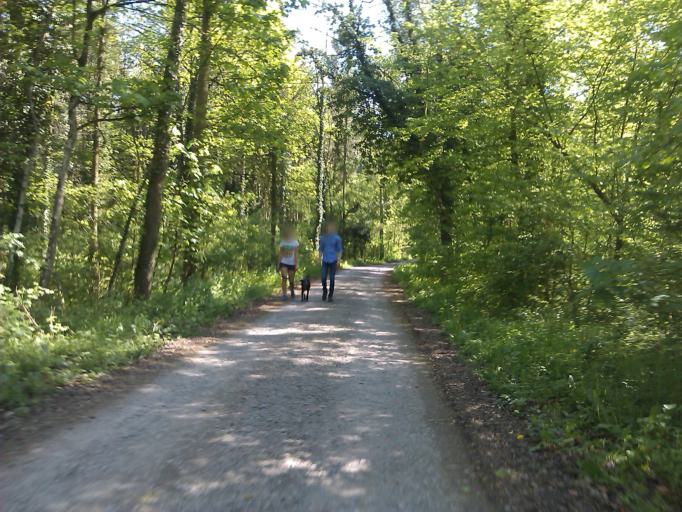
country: DE
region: Baden-Wuerttemberg
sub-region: Karlsruhe Region
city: Sulzfeld
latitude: 49.0894
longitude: 8.8656
